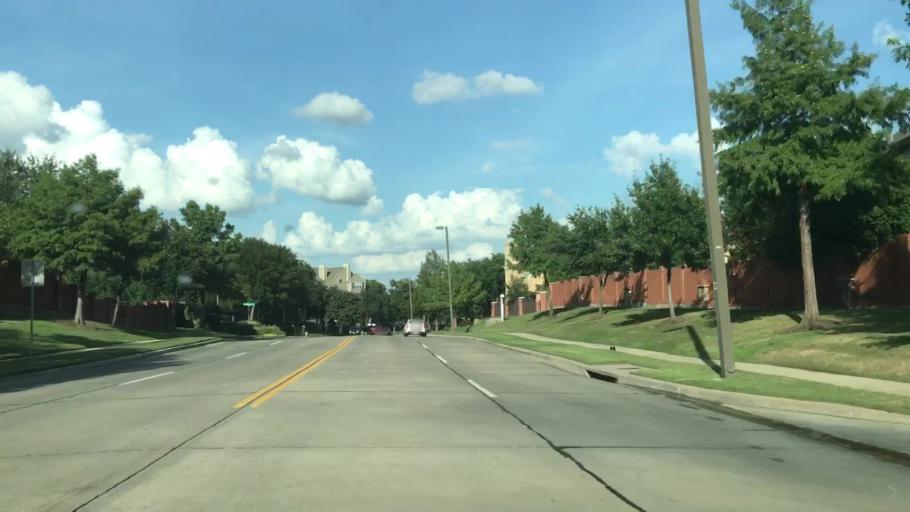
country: US
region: Texas
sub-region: Dallas County
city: Coppell
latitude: 32.9463
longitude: -96.9601
